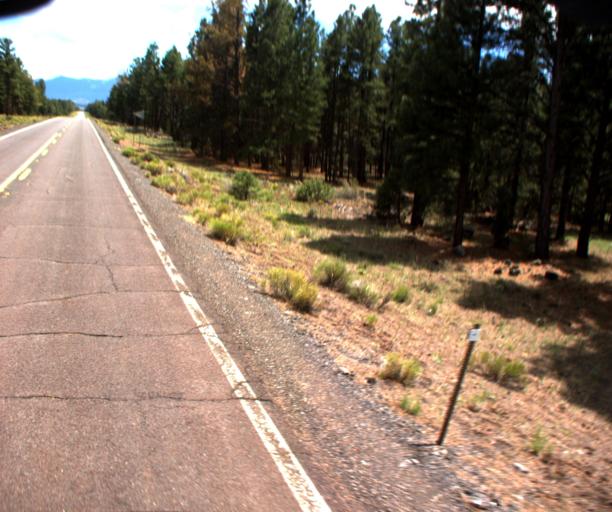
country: US
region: Arizona
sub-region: Coconino County
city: Parks
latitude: 35.4852
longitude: -111.8048
